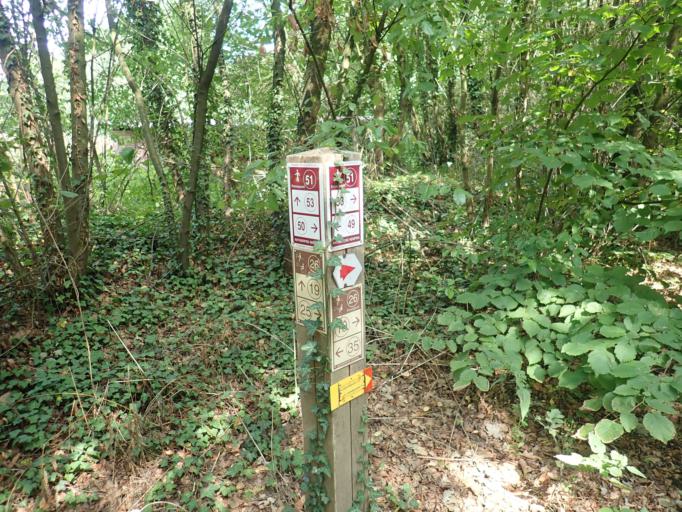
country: BE
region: Flanders
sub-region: Provincie Antwerpen
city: Meerhout
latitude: 51.1690
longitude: 5.0756
